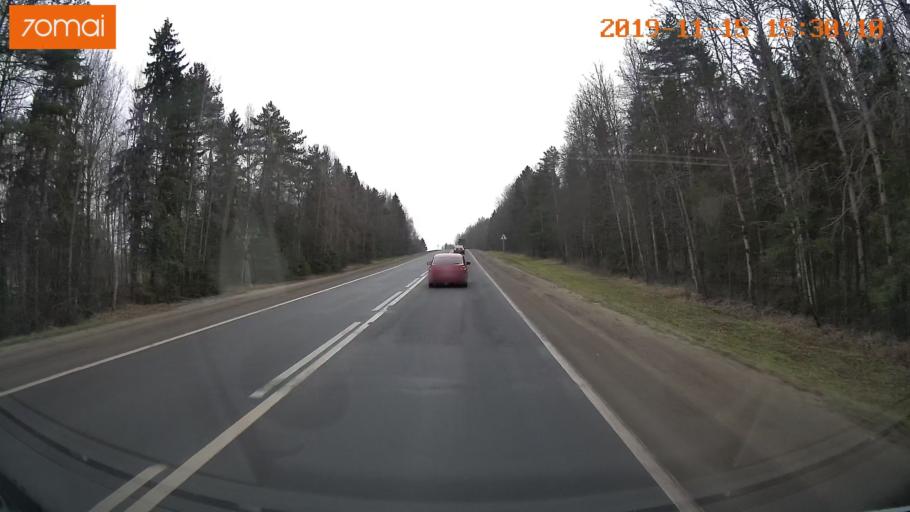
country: RU
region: Jaroslavl
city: Danilov
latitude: 58.1127
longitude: 40.1147
